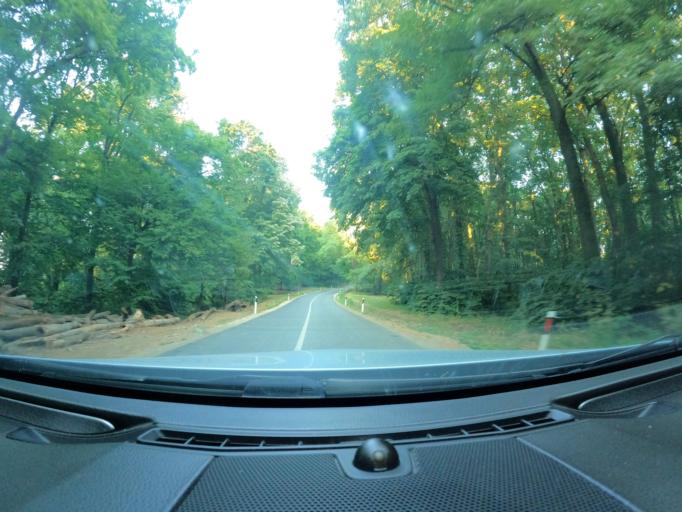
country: RS
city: Vrdnik
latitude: 45.1566
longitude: 19.8054
